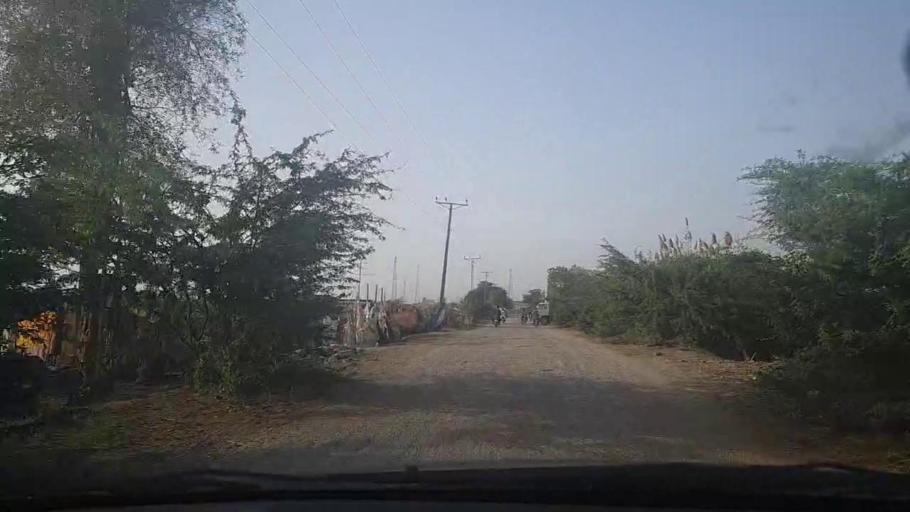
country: PK
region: Sindh
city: Keti Bandar
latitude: 24.2945
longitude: 67.6082
